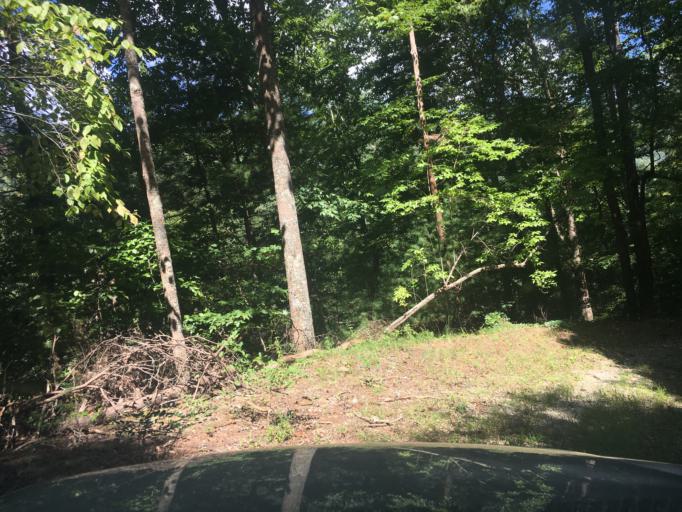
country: US
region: North Carolina
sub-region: Graham County
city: Robbinsville
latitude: 35.2701
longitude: -83.6823
